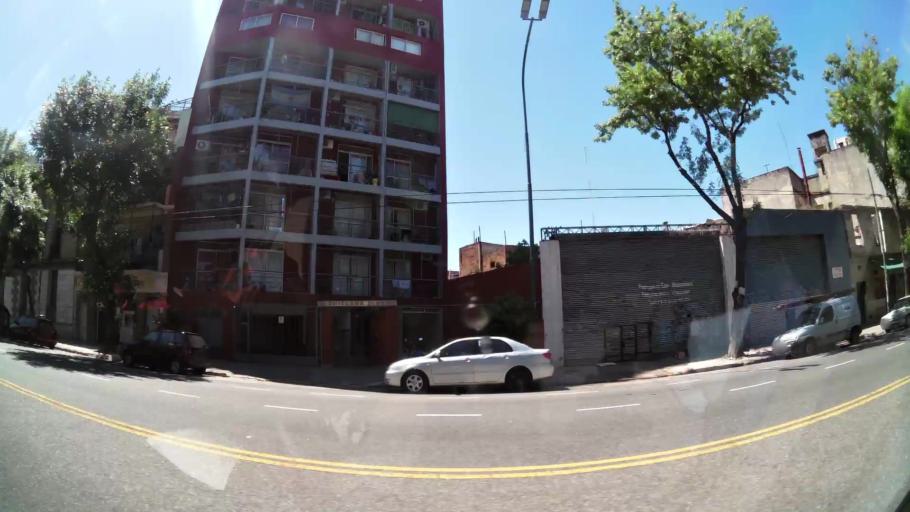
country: AR
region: Buenos Aires F.D.
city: Buenos Aires
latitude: -34.6284
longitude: -58.4048
